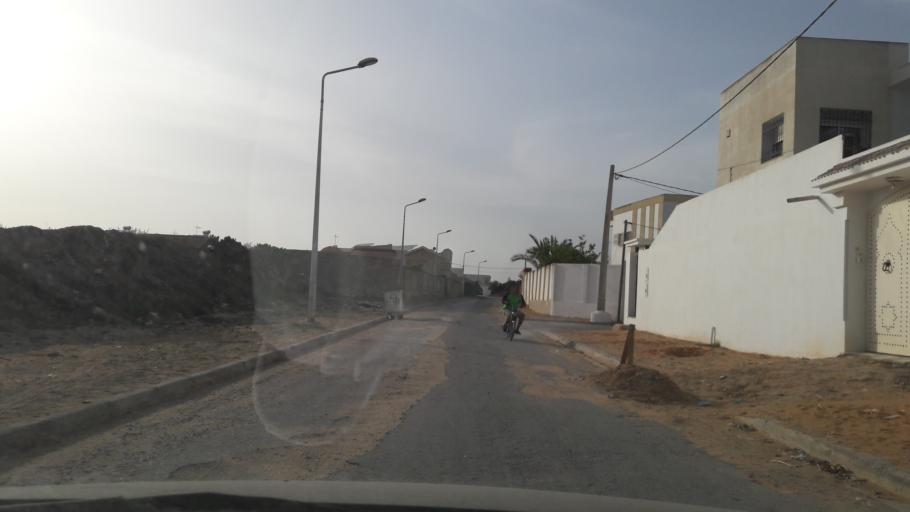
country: TN
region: Safaqis
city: Al Qarmadah
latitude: 34.8013
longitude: 10.7524
